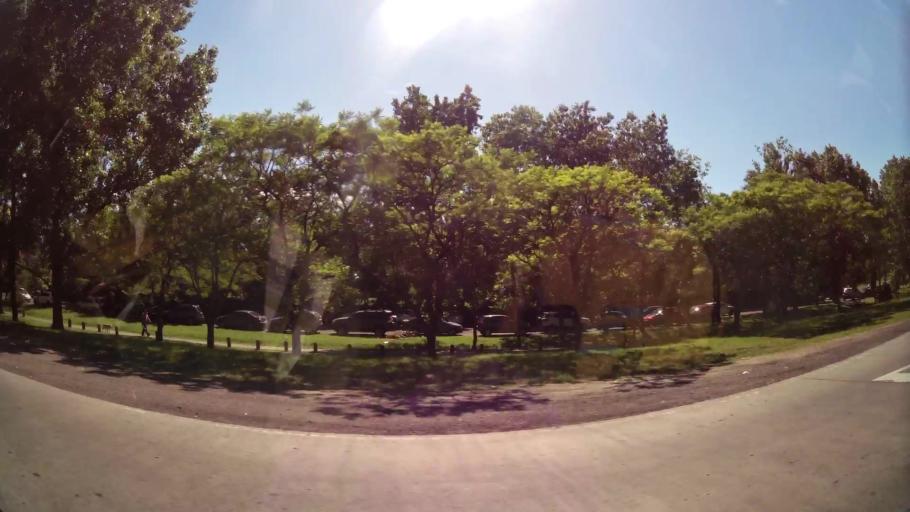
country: AR
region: Buenos Aires
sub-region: Partido de San Isidro
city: San Isidro
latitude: -34.4822
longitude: -58.5611
